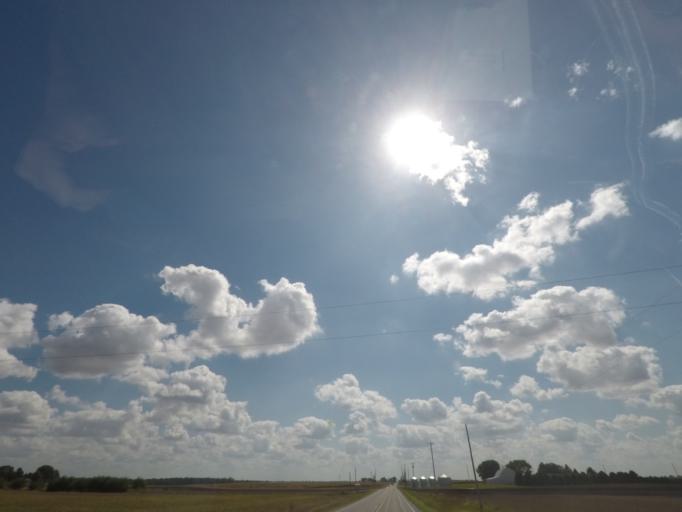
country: US
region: Iowa
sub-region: Story County
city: Nevada
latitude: 42.0260
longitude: -93.4058
